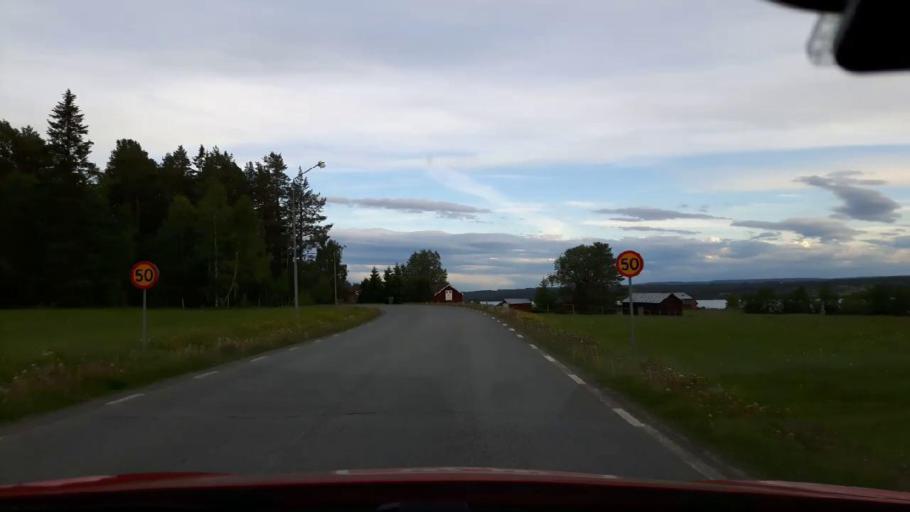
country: SE
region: Jaemtland
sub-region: OEstersunds Kommun
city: Ostersund
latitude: 63.0540
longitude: 14.4504
